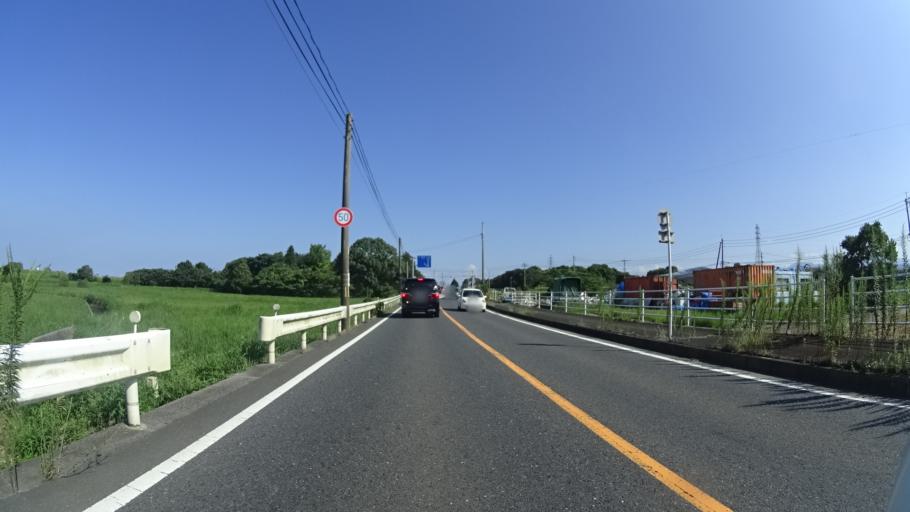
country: JP
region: Fukuoka
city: Tsuiki
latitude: 33.6725
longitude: 131.0164
